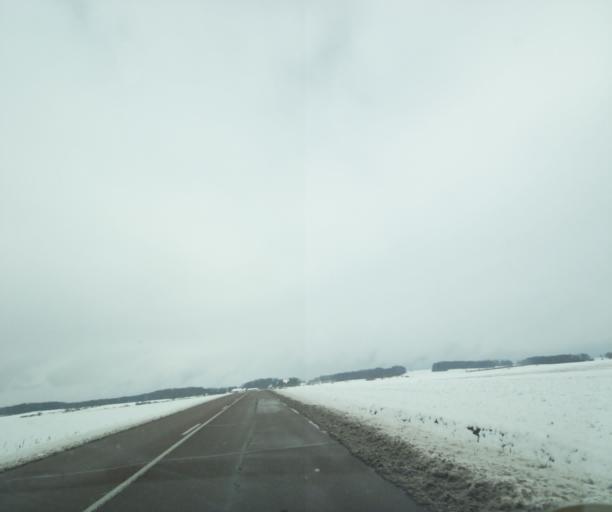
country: FR
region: Champagne-Ardenne
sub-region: Departement de la Haute-Marne
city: Montier-en-Der
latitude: 48.4397
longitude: 4.7305
